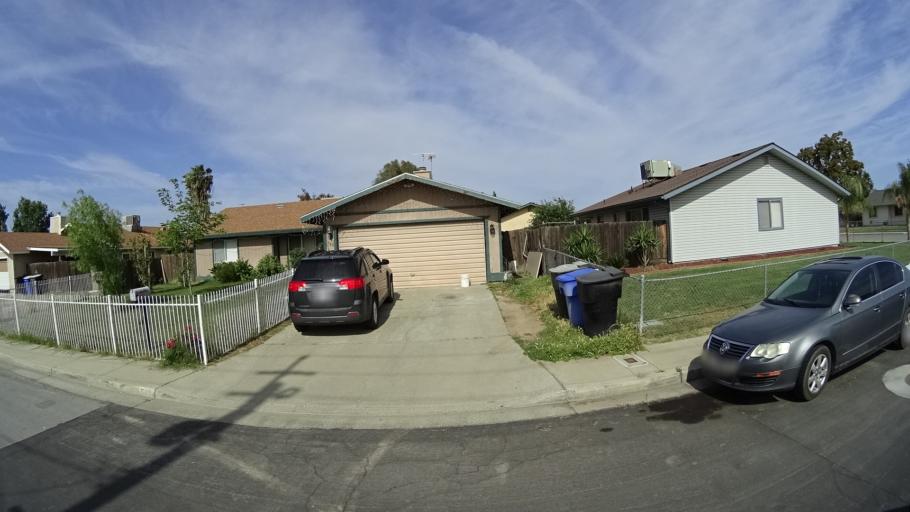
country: US
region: California
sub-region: Kings County
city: Hanford
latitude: 36.3188
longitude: -119.6617
